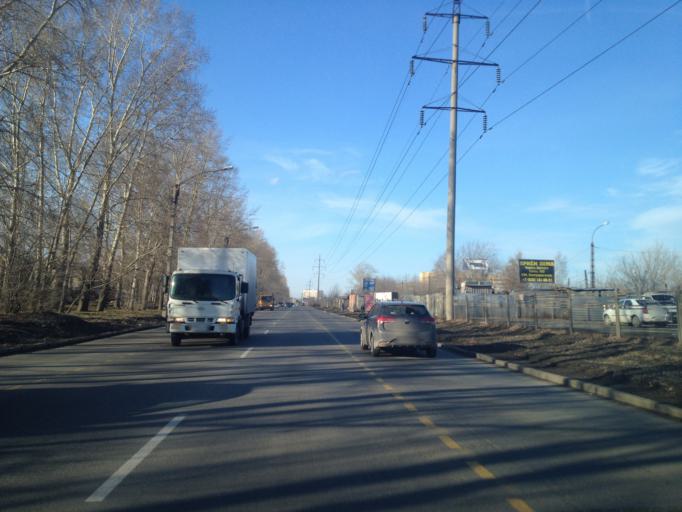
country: RU
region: Sverdlovsk
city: Sovkhoznyy
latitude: 56.7654
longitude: 60.5926
